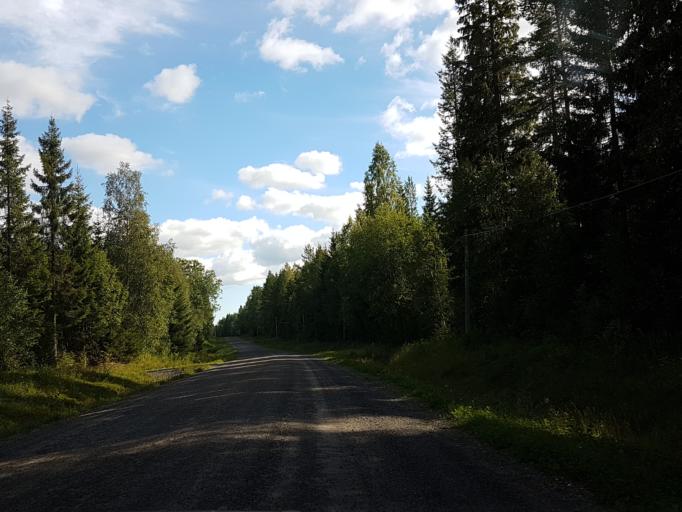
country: SE
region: Vaesterbotten
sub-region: Robertsfors Kommun
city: Robertsfors
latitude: 64.1702
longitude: 20.6460
